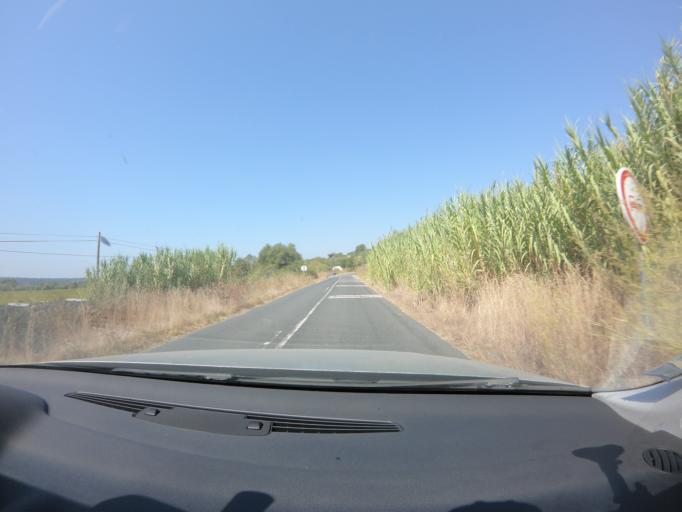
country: PT
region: Setubal
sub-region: Alcacer do Sal
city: Alcacer do Sal
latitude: 38.2870
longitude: -8.4041
